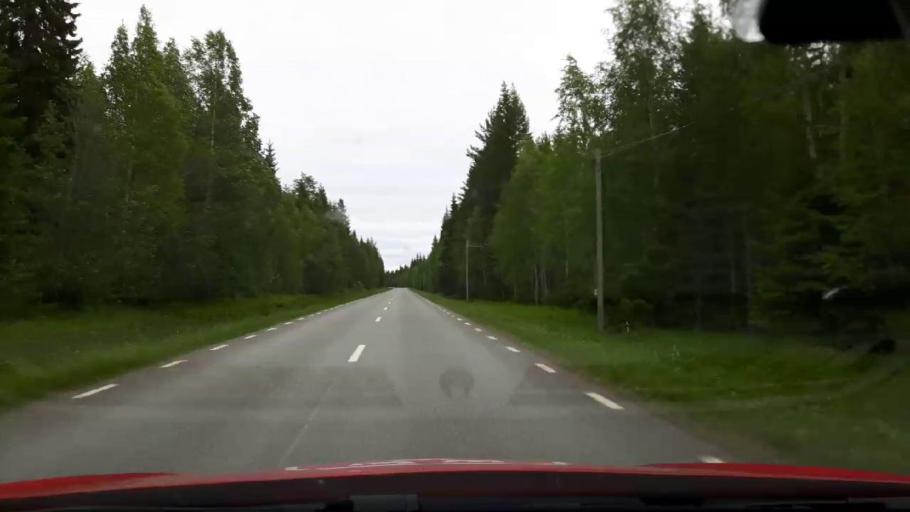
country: SE
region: Jaemtland
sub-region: Stroemsunds Kommun
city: Stroemsund
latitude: 63.4038
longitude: 15.6245
